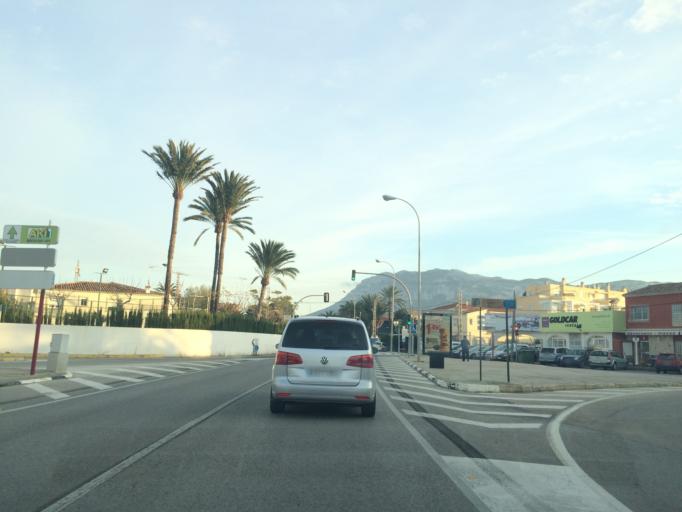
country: ES
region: Valencia
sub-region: Provincia de Alicante
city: Denia
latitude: 38.8517
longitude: 0.0929
